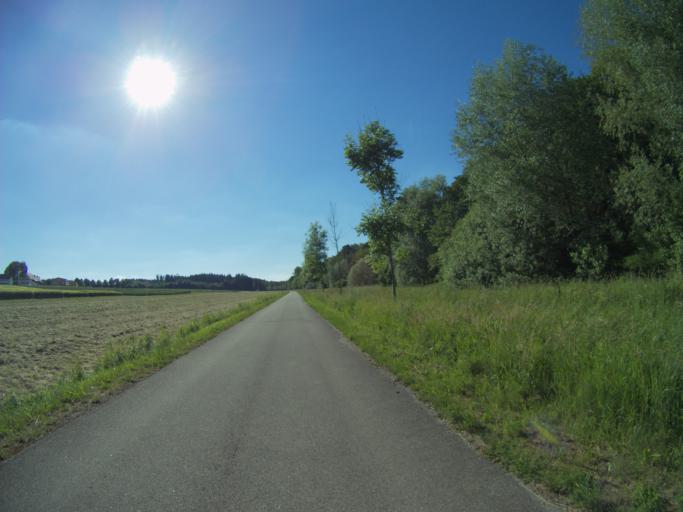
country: DE
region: Bavaria
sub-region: Upper Bavaria
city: Freising
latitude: 48.4066
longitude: 11.6990
